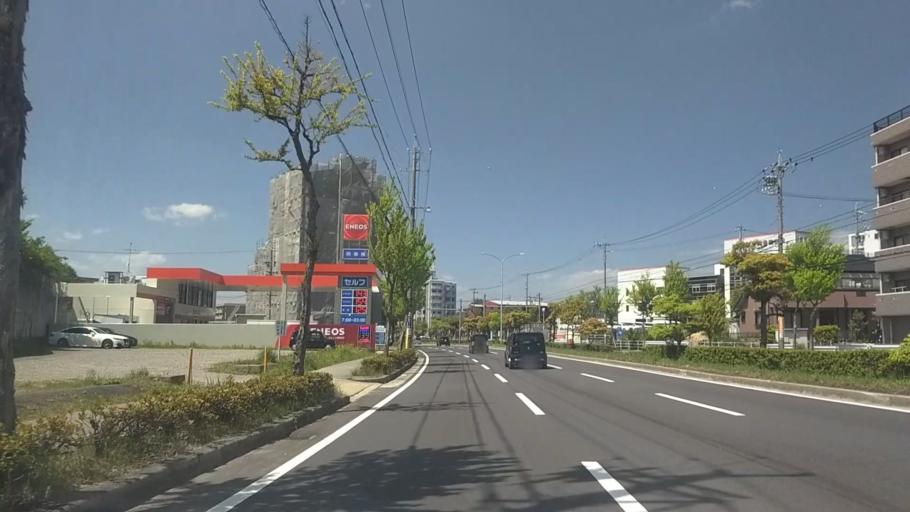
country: JP
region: Aichi
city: Okazaki
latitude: 34.9569
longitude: 137.1897
